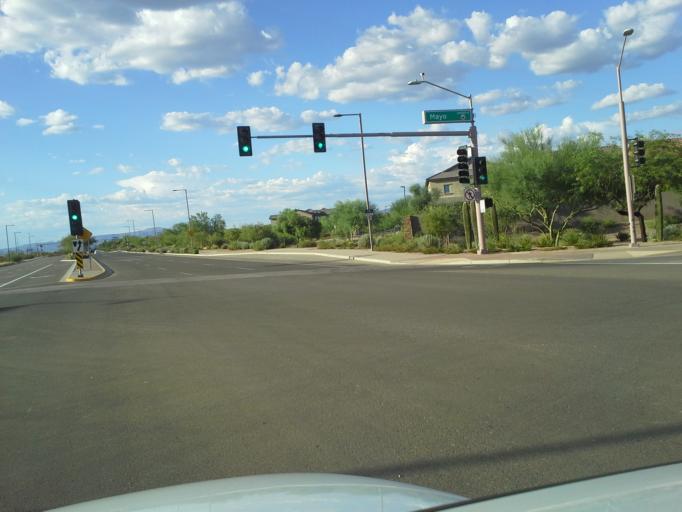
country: US
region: Arizona
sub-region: Maricopa County
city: Cave Creek
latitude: 33.6807
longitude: -112.0051
